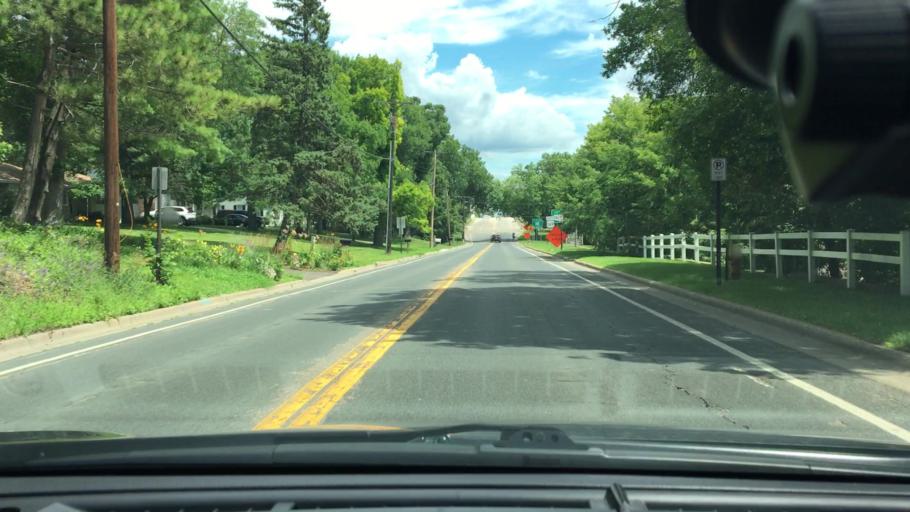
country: US
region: Minnesota
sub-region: Hennepin County
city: New Hope
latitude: 45.0075
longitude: -93.4053
